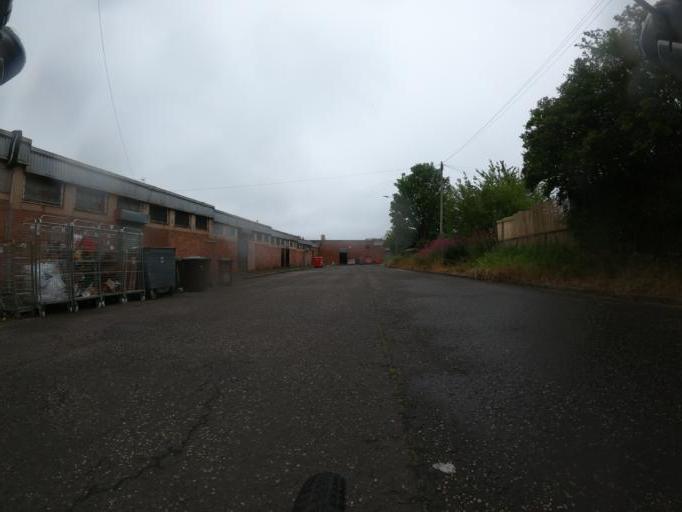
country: GB
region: Scotland
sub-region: Edinburgh
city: Edinburgh
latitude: 55.9672
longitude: -3.2456
